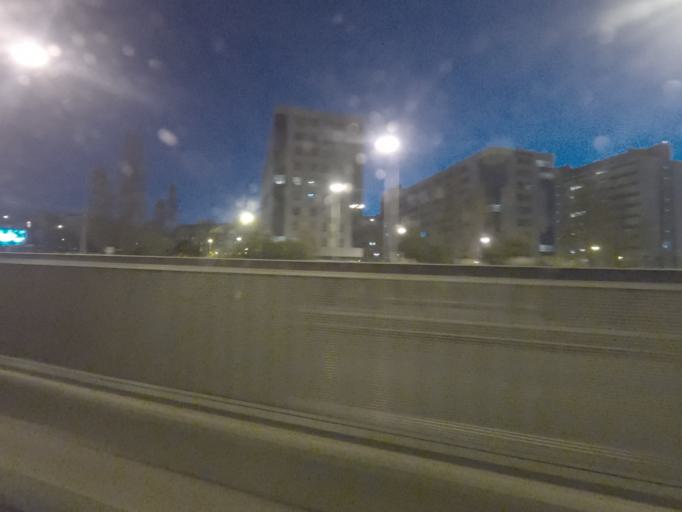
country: PT
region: Porto
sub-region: Matosinhos
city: Senhora da Hora
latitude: 41.1661
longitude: -8.6407
